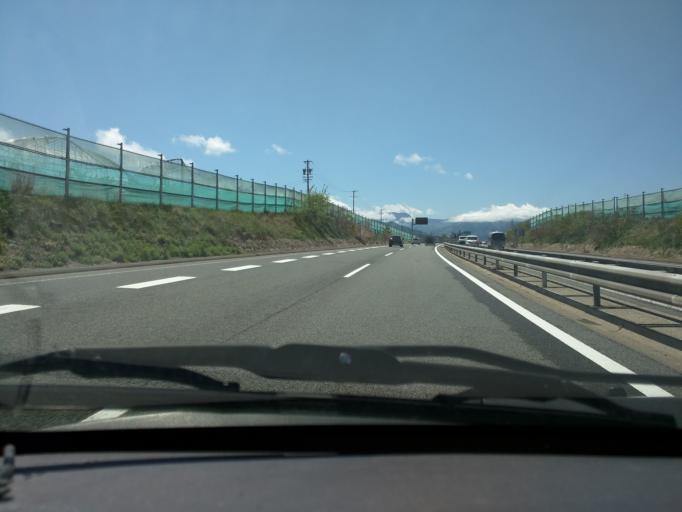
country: JP
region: Nagano
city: Nakano
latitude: 36.7364
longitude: 138.3178
